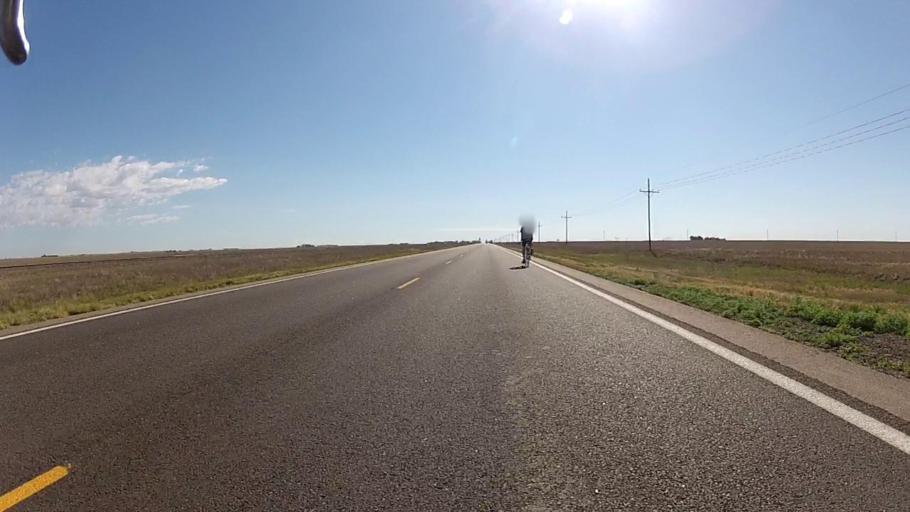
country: US
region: Kansas
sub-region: Gray County
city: Cimarron
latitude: 37.5826
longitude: -100.5022
